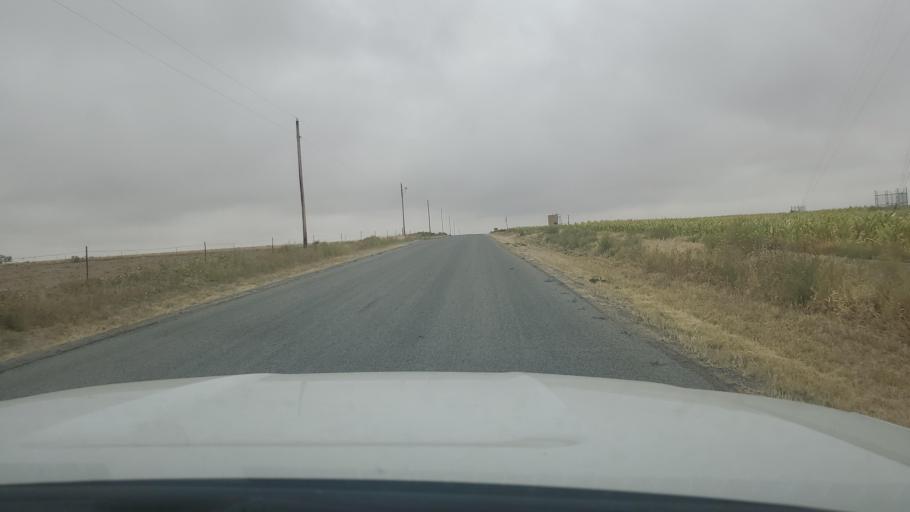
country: US
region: Colorado
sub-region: Weld County
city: Lochbuie
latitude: 39.9185
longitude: -104.6031
